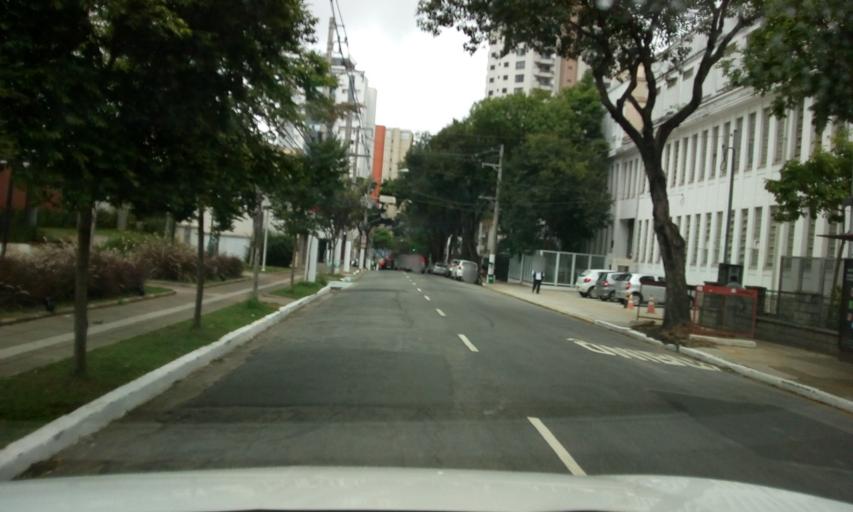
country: BR
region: Sao Paulo
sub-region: Sao Paulo
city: Sao Paulo
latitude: -23.5856
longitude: -46.6400
